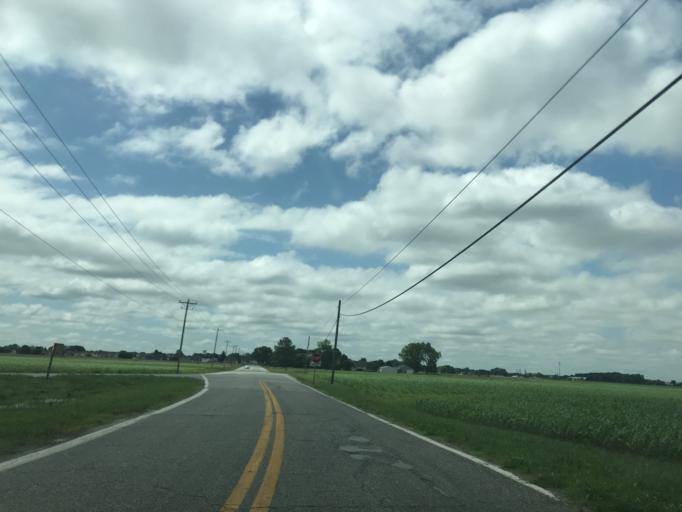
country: US
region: Maryland
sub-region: Caroline County
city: Ridgely
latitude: 38.9600
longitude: -75.8906
